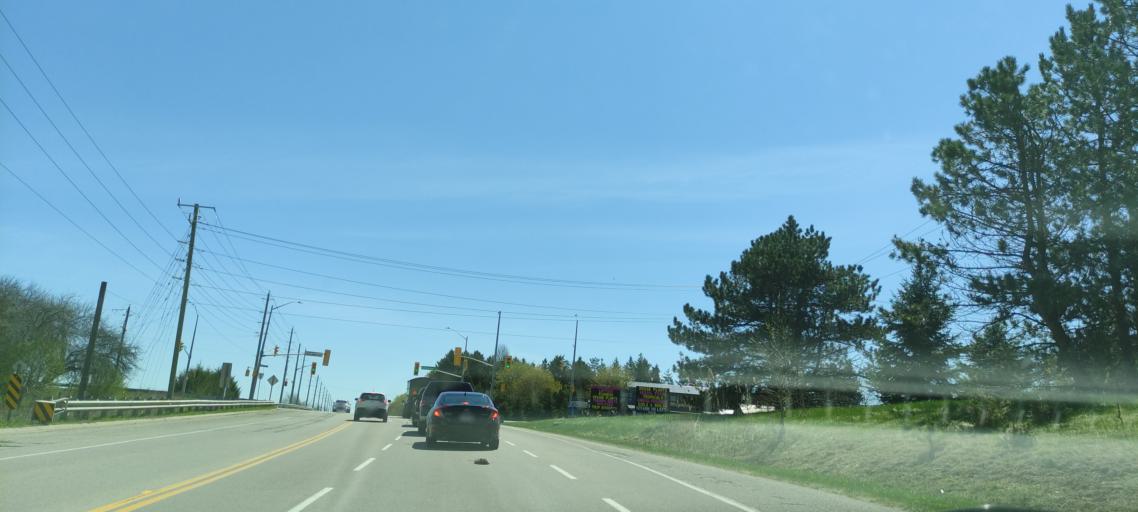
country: CA
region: Ontario
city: Waterloo
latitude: 43.5870
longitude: -80.4678
